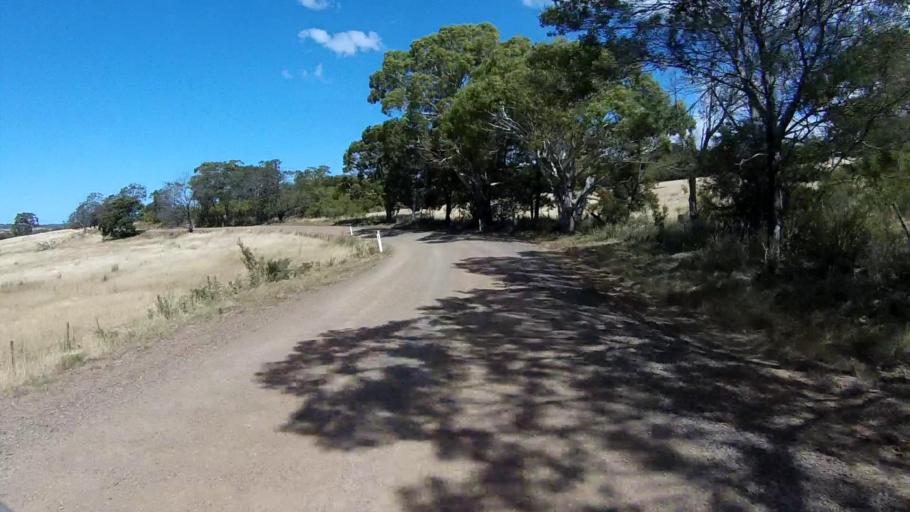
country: AU
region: Tasmania
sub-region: Break O'Day
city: St Helens
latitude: -41.9716
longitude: 148.0727
